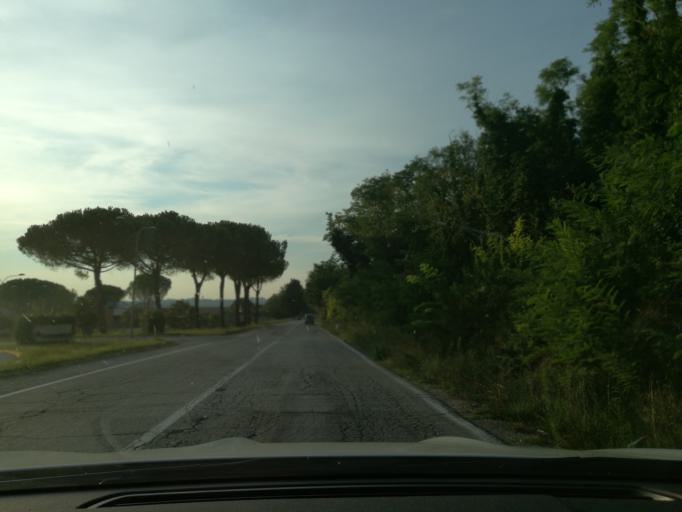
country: IT
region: Umbria
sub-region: Provincia di Terni
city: San Gemini
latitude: 42.6329
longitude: 12.5520
